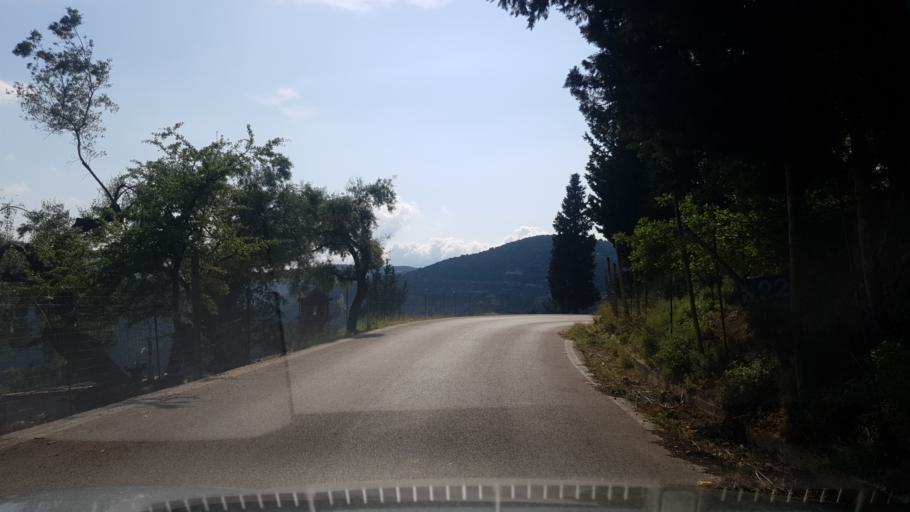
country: GR
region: Ionian Islands
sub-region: Lefkada
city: Nidri
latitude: 38.6525
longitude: 20.7070
